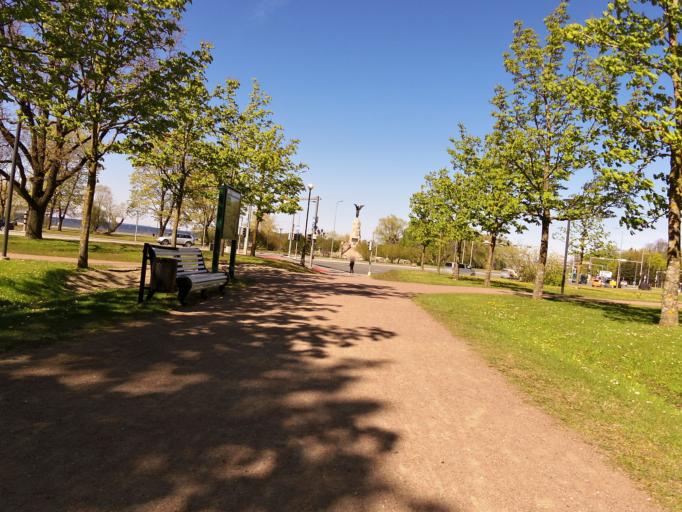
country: EE
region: Harju
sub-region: Tallinna linn
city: Tallinn
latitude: 59.4422
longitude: 24.7932
